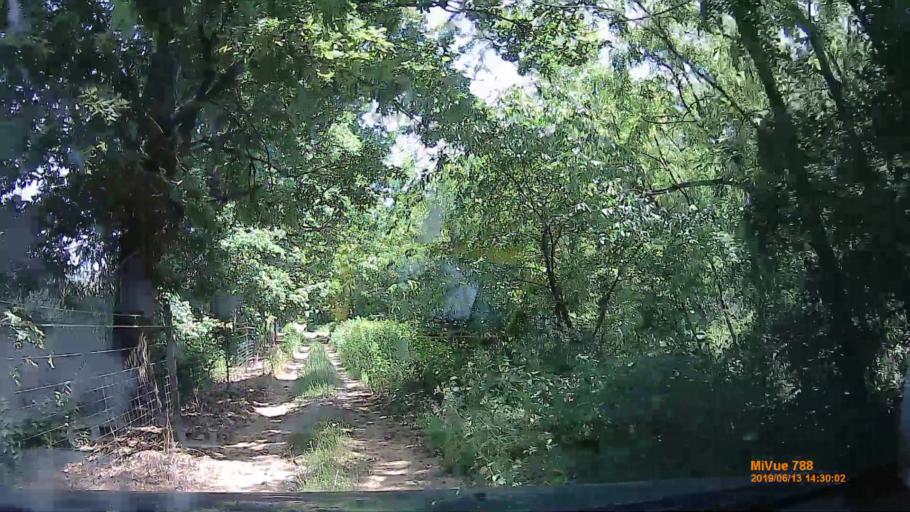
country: HU
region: Pest
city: Szada
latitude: 47.6025
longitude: 19.3058
